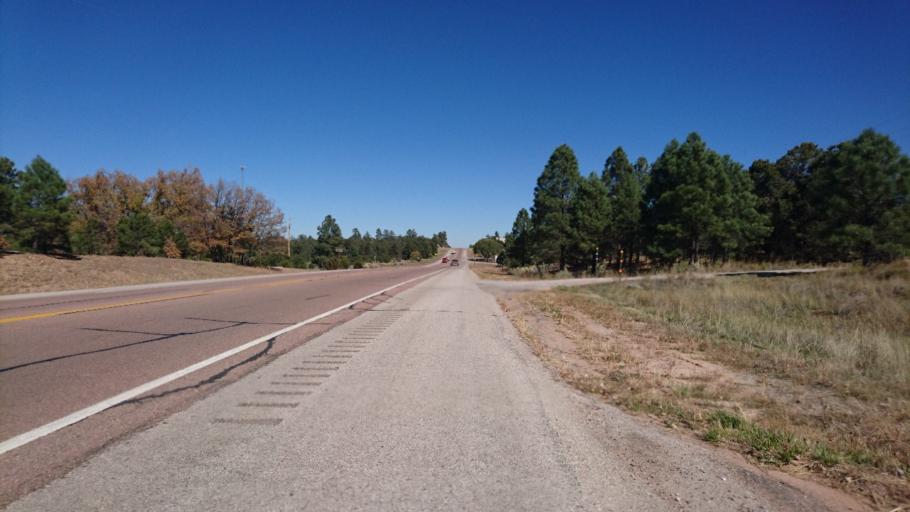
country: US
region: New Mexico
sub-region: McKinley County
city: Black Rock
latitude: 35.2457
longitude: -108.7607
